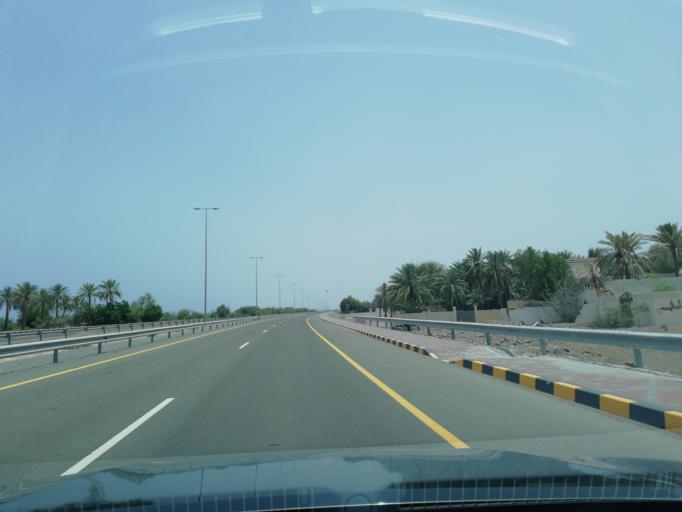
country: OM
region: Al Batinah
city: Shinas
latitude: 24.7845
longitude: 56.4564
